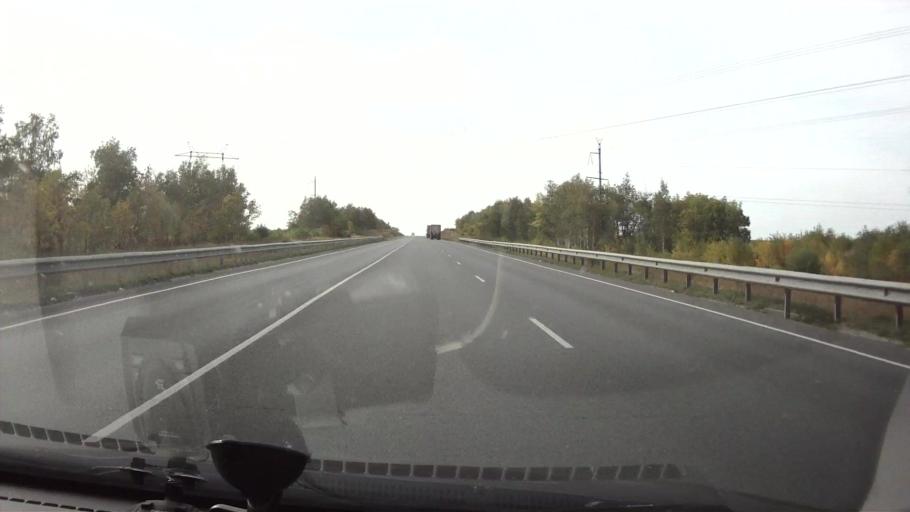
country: RU
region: Saratov
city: Tersa
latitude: 52.1011
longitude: 47.5127
